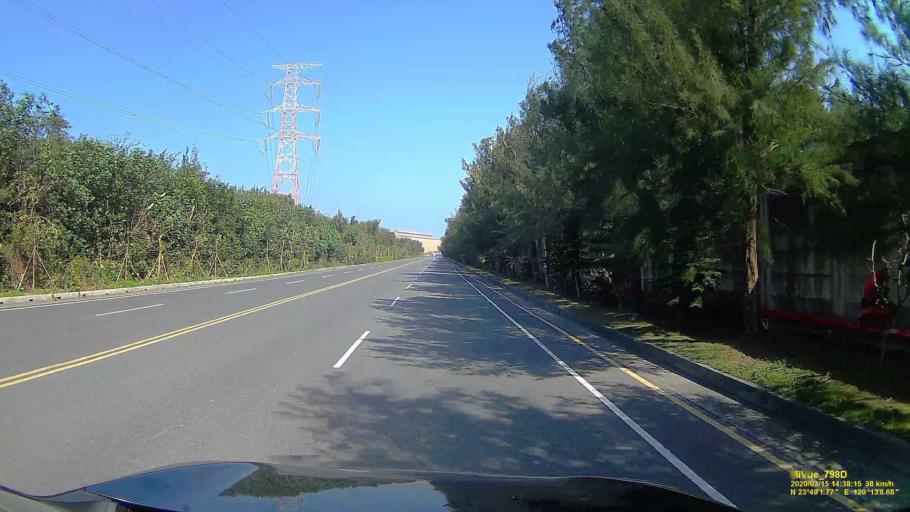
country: TW
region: Taiwan
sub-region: Yunlin
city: Douliu
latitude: 23.8171
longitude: 120.2193
